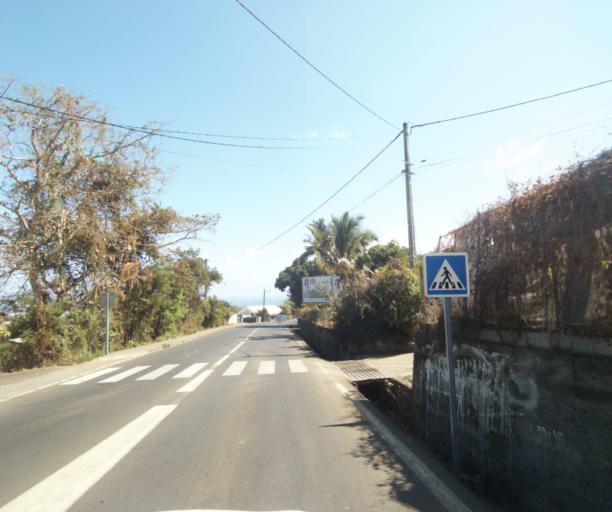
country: RE
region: Reunion
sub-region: Reunion
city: La Possession
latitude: -20.9848
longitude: 55.3340
